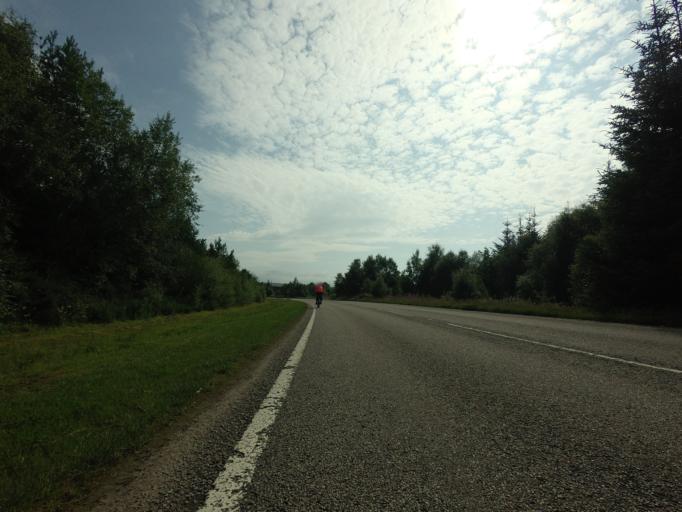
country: GB
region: Scotland
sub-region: Highland
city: Evanton
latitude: 57.9260
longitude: -4.4008
